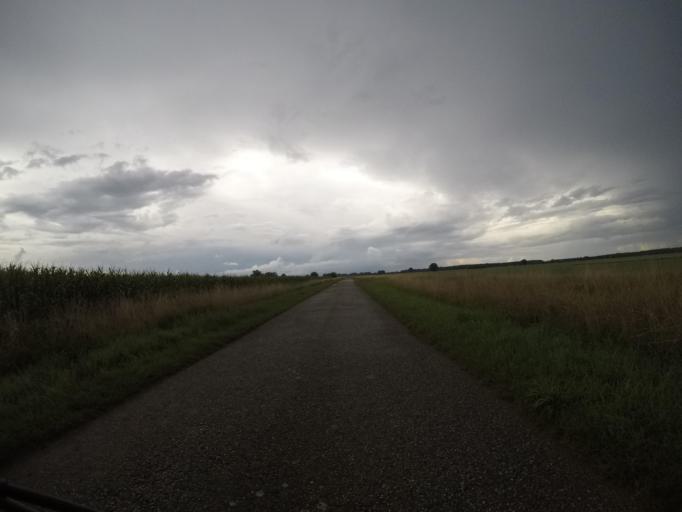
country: DE
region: Lower Saxony
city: Neu Darchau
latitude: 53.2517
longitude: 10.9008
